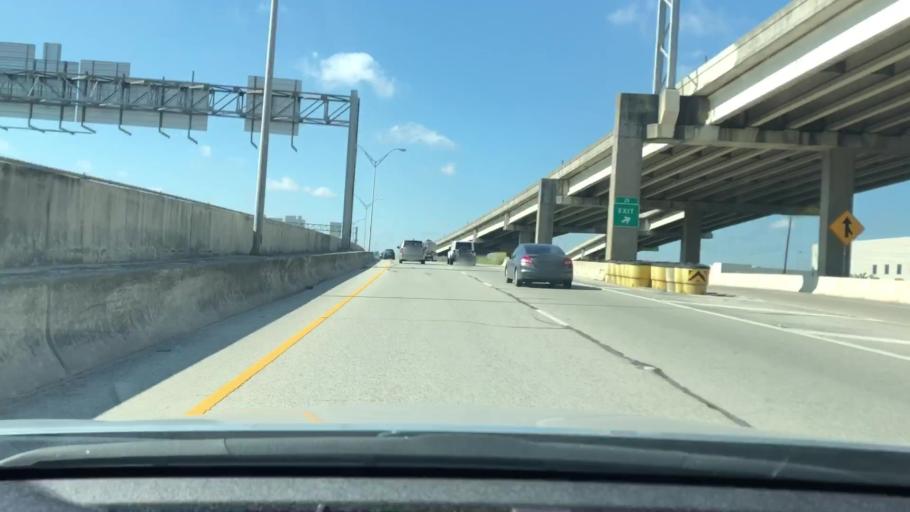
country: US
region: Texas
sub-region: Bexar County
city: Windcrest
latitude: 29.5200
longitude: -98.3976
